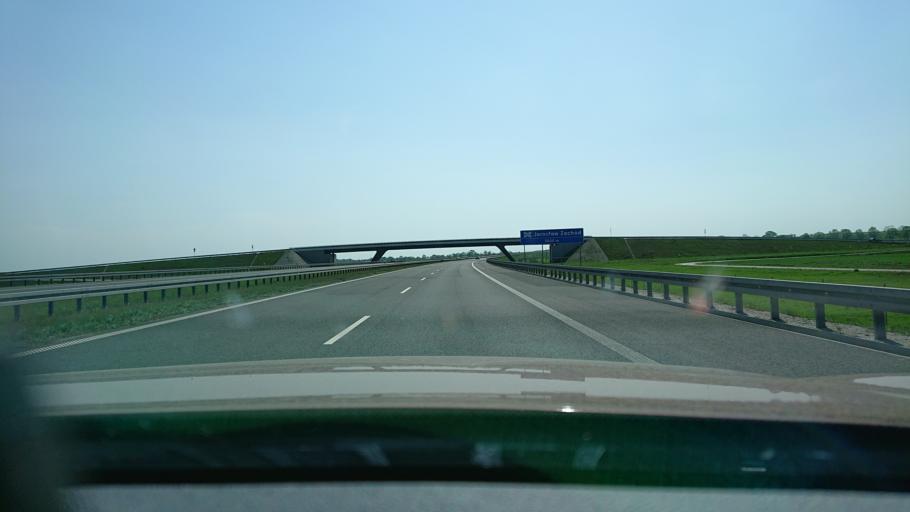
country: PL
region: Subcarpathian Voivodeship
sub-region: Powiat przeworski
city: Rozborz
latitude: 50.0732
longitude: 22.5476
